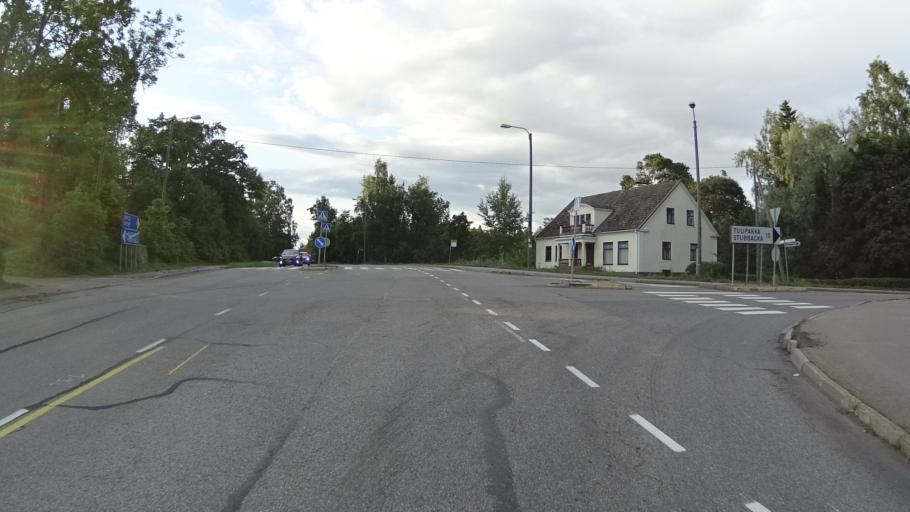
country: FI
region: Uusimaa
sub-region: Helsinki
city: Nurmijaervi
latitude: 60.3476
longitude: 24.8652
